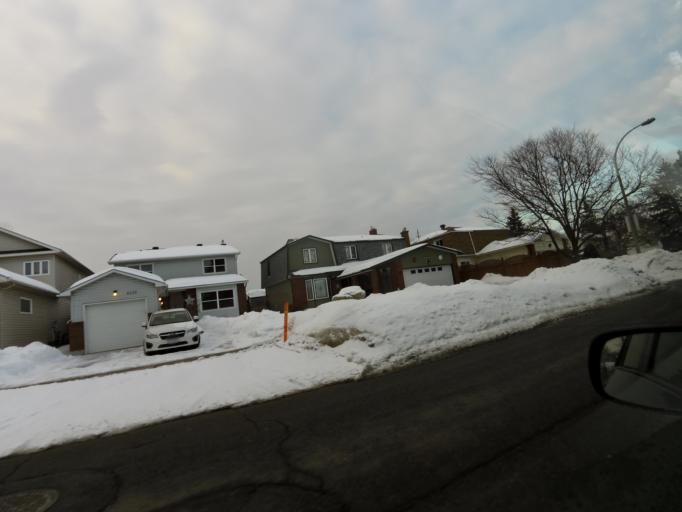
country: CA
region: Quebec
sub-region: Outaouais
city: Gatineau
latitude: 45.4731
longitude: -75.5393
